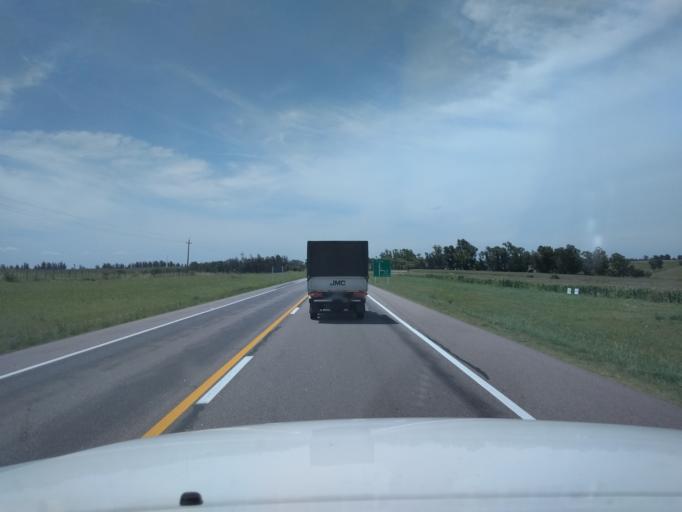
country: UY
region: Florida
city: Florida
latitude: -34.1371
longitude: -56.1829
